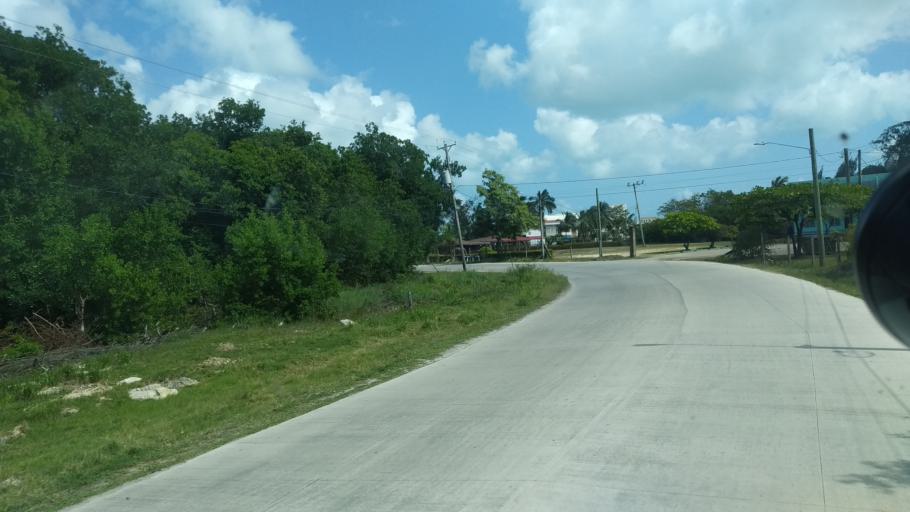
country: BZ
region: Belize
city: Belize City
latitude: 17.5110
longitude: -88.1999
